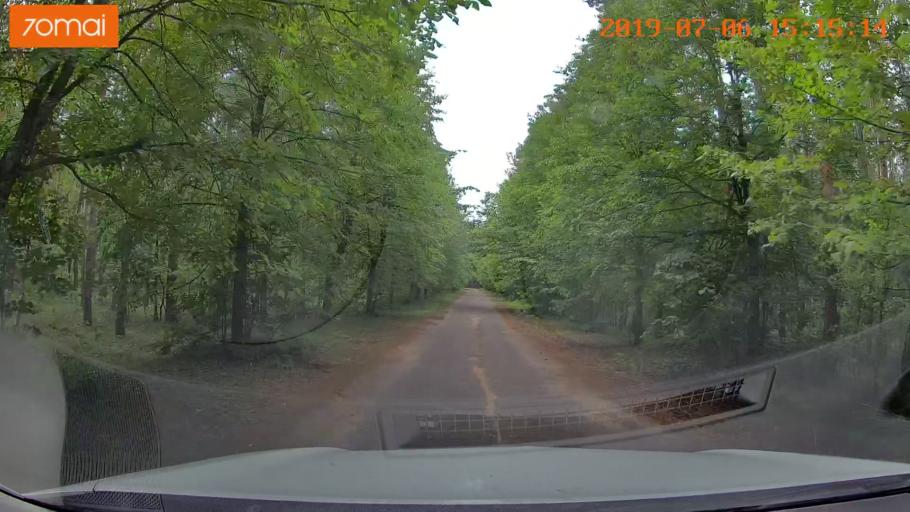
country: BY
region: Minsk
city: Ivyanyets
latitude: 53.9761
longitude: 26.6863
